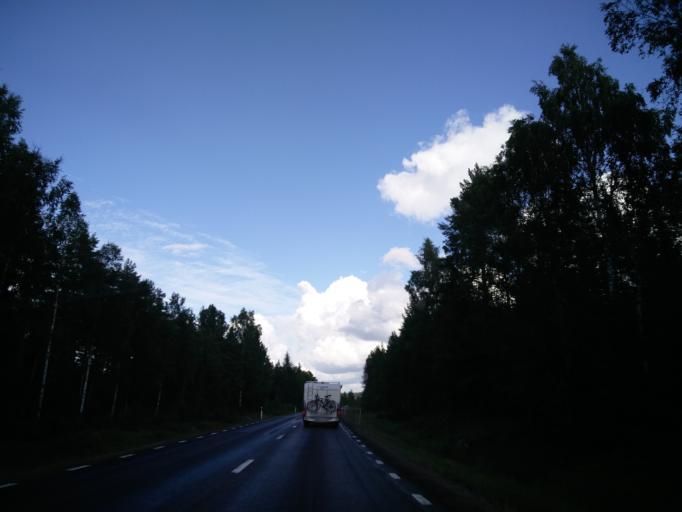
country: SE
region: Vaermland
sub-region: Hagfors Kommun
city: Ekshaerad
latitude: 60.4787
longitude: 13.3526
